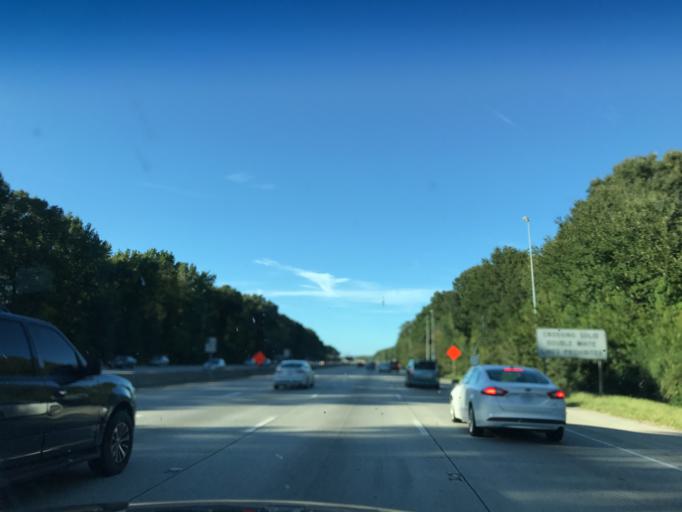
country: US
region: Virginia
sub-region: City of Chesapeake
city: Chesapeake
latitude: 36.8138
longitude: -76.1946
